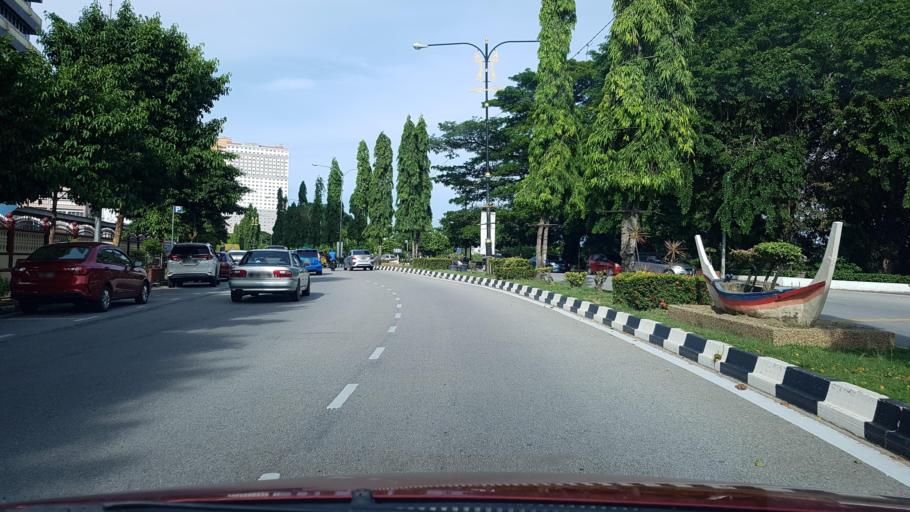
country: MY
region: Terengganu
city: Kuala Terengganu
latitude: 5.3280
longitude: 103.1422
